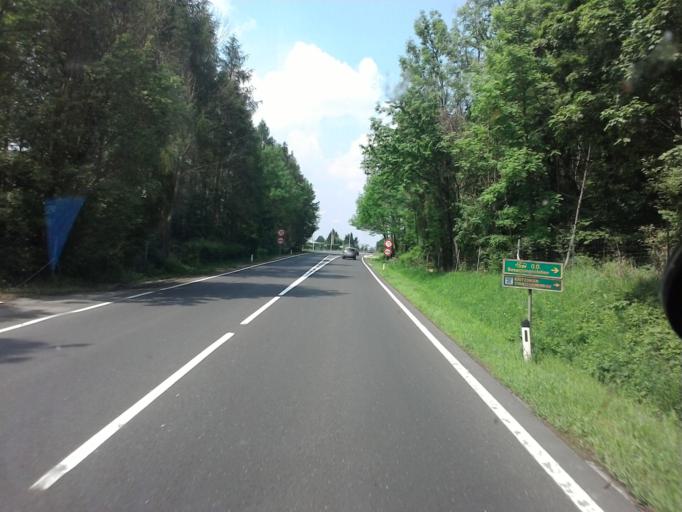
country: AT
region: Upper Austria
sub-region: Wels-Land
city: Steinhaus
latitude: 48.1000
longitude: 14.0403
